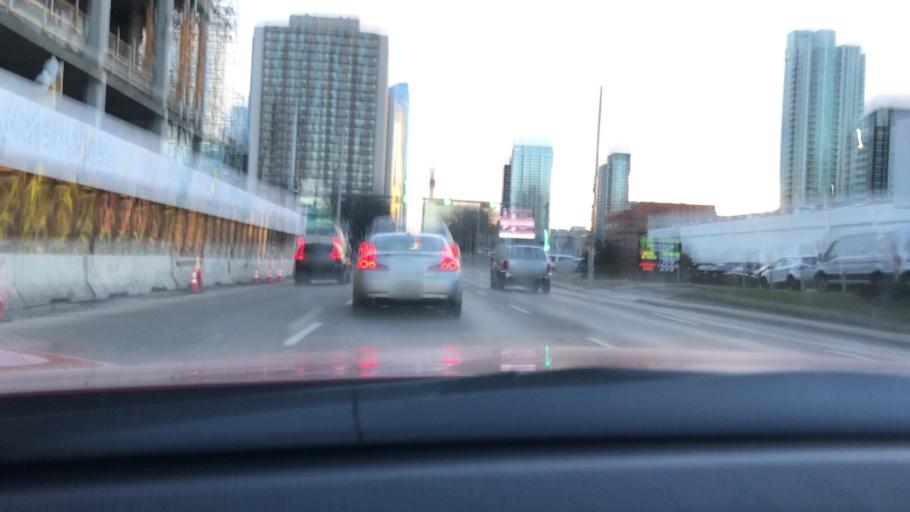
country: CA
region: Alberta
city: Calgary
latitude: 51.0453
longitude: -114.0870
